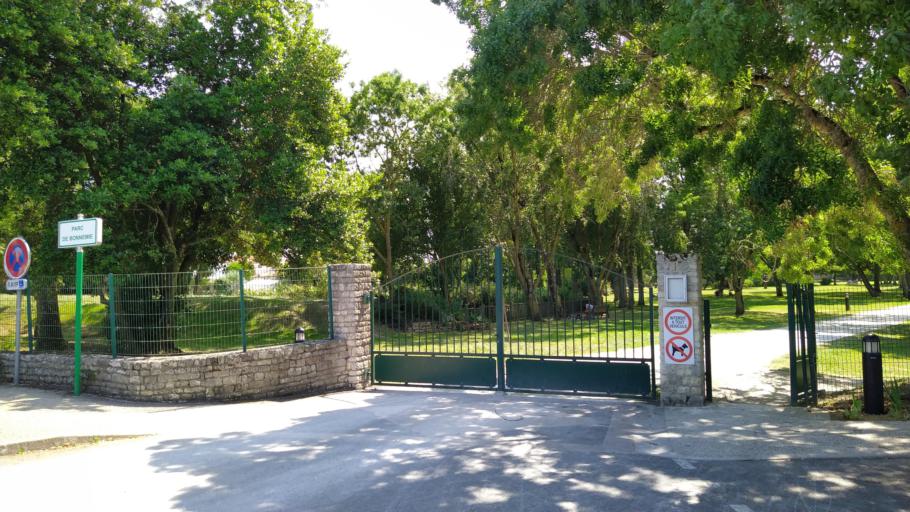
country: FR
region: Poitou-Charentes
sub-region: Departement de la Charente-Maritime
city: Dolus-d'Oleron
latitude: 45.9446
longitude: -1.3145
